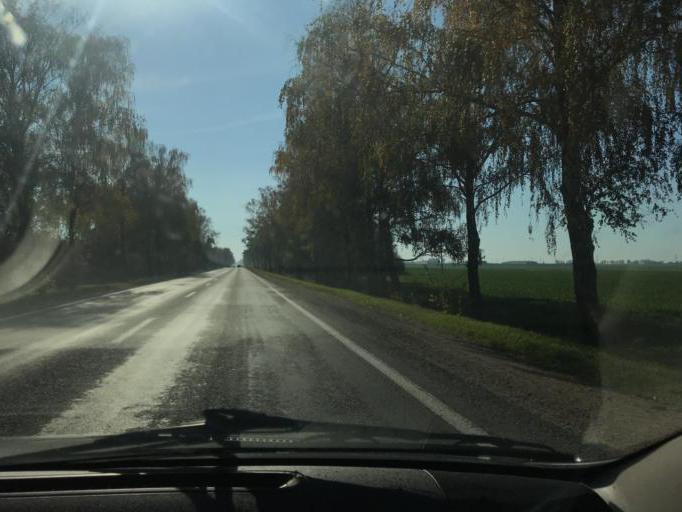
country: BY
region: Minsk
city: Salihorsk
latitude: 52.8189
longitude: 27.4653
